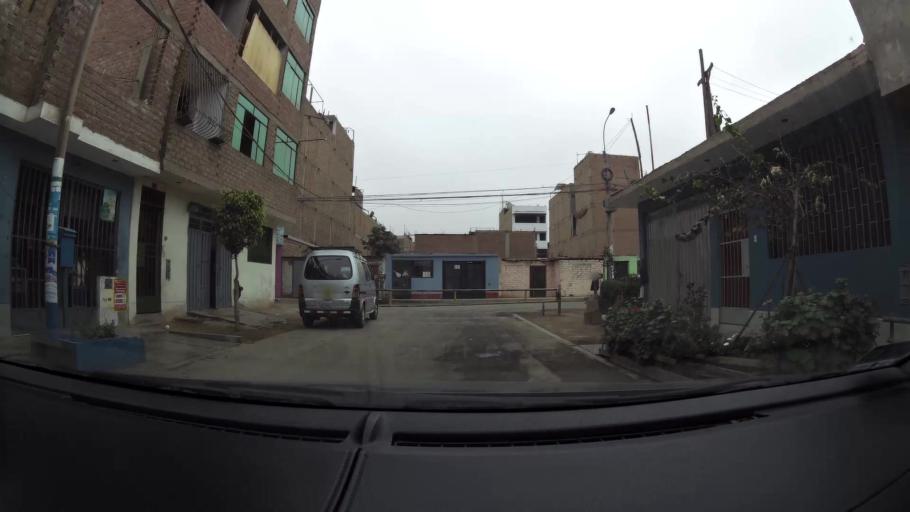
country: PE
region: Lima
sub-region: Lima
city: Independencia
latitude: -11.9603
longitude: -77.0824
